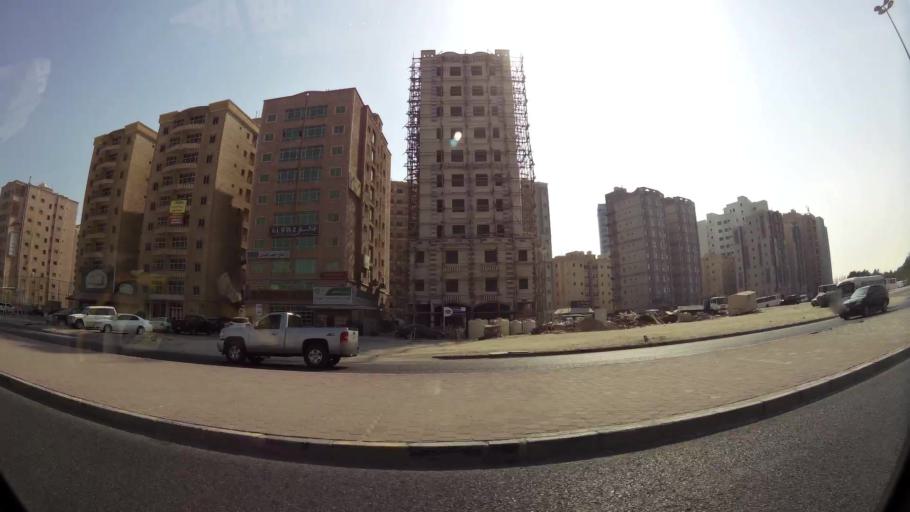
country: KW
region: Al Ahmadi
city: Al Fintas
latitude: 29.1611
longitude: 48.1146
